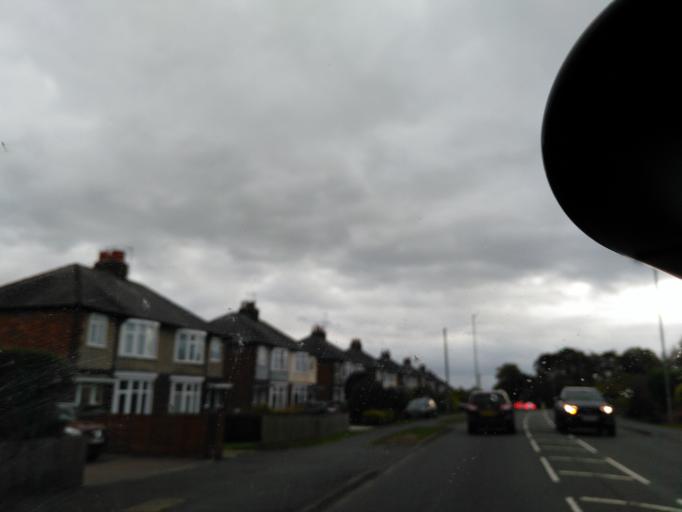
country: GB
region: England
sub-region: North Yorkshire
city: Northallerton
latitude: 54.3304
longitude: -1.4431
